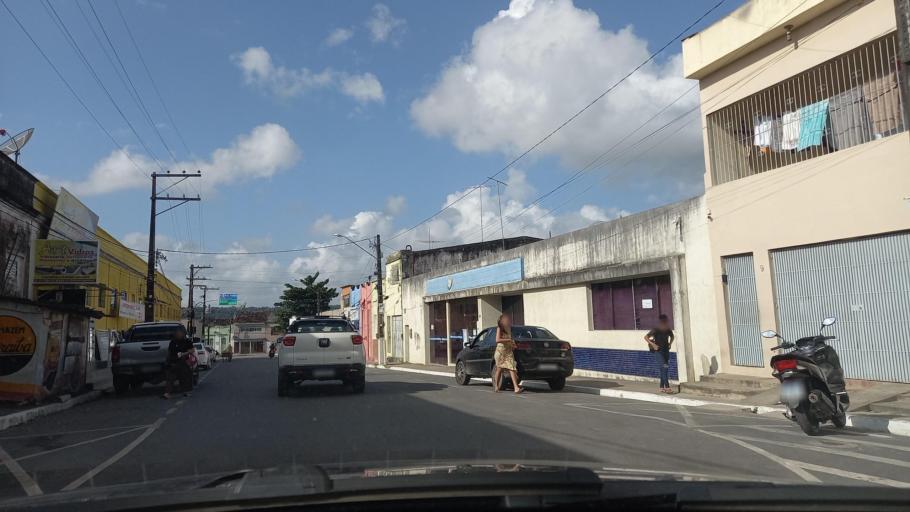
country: BR
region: Pernambuco
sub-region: Goiana
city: Goiana
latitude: -7.5590
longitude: -34.9972
